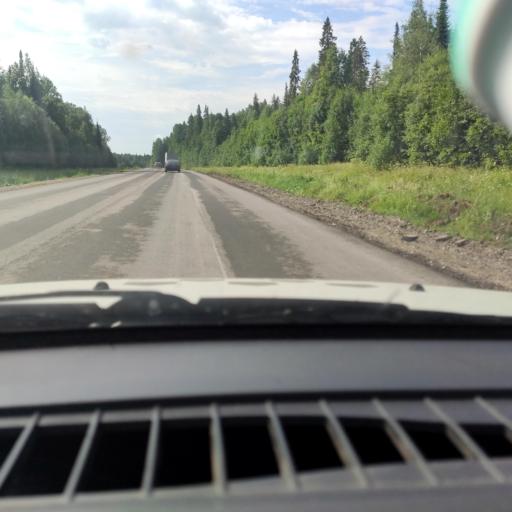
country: RU
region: Perm
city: Siva
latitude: 58.4667
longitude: 54.4064
